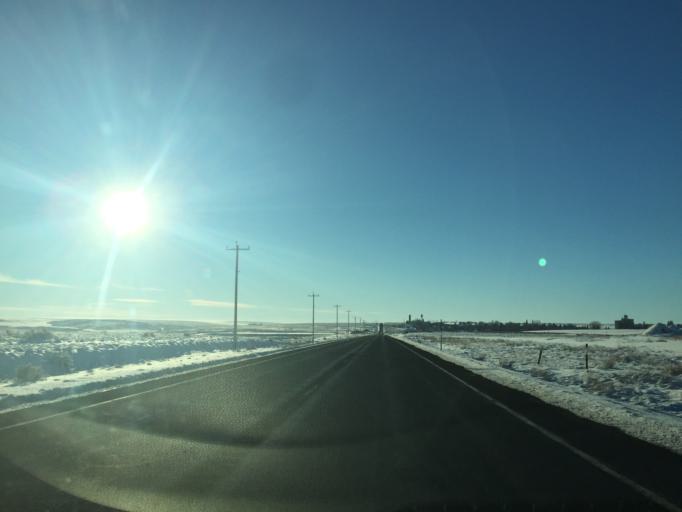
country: US
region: Washington
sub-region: Okanogan County
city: Coulee Dam
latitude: 47.7136
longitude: -118.9172
